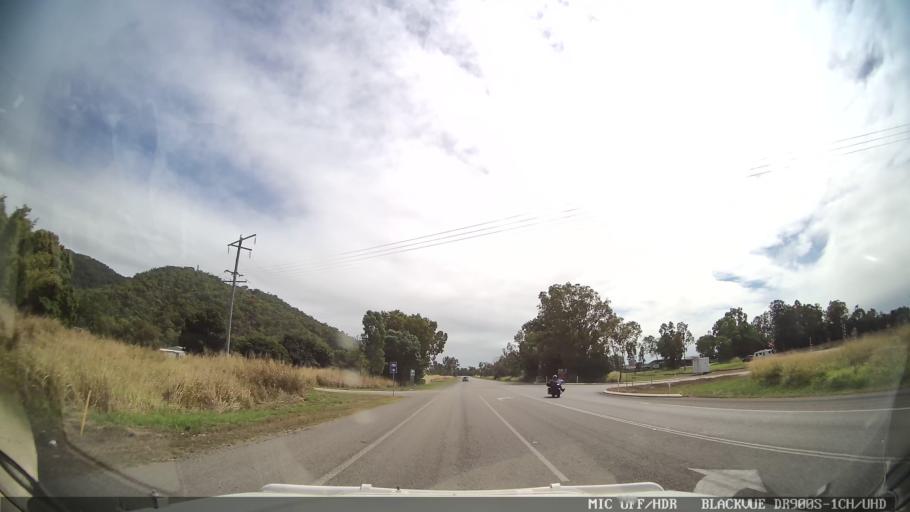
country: AU
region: Queensland
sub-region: Hinchinbrook
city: Ingham
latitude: -19.0162
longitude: 146.3664
